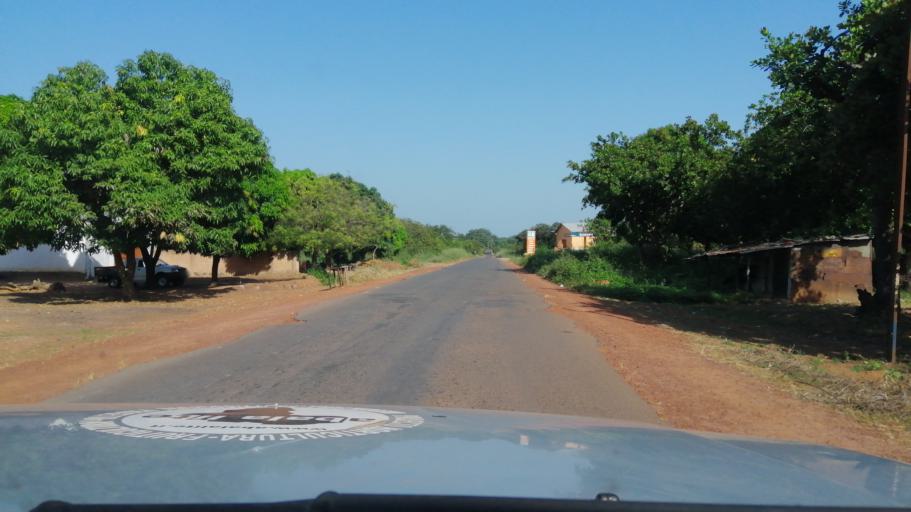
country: GW
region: Bissau
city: Bissau
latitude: 11.9589
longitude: -15.5352
